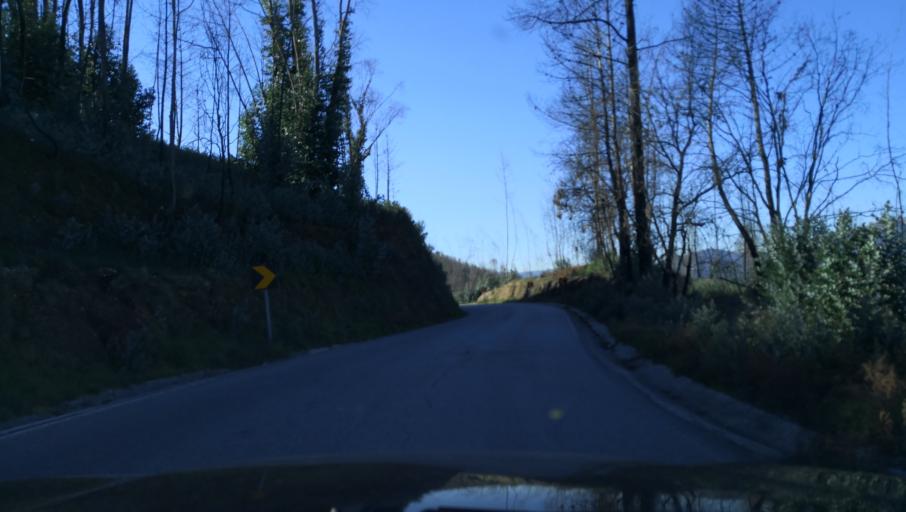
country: PT
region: Viseu
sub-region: Vouzela
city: Vouzela
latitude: 40.7274
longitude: -8.1292
